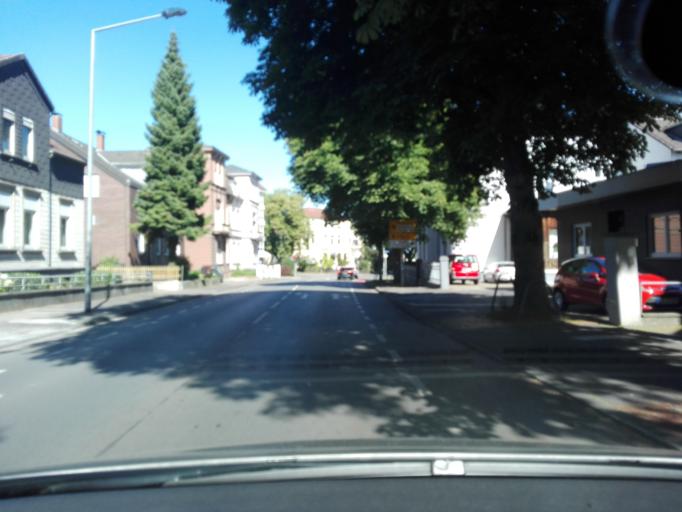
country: DE
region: North Rhine-Westphalia
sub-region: Regierungsbezirk Arnsberg
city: Unna
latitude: 51.5434
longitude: 7.6834
